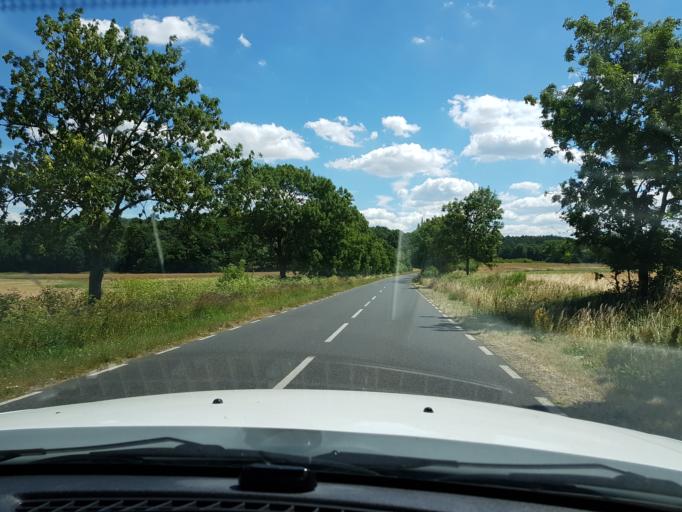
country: PL
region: West Pomeranian Voivodeship
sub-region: Powiat mysliborski
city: Mysliborz
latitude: 52.9143
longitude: 14.9122
